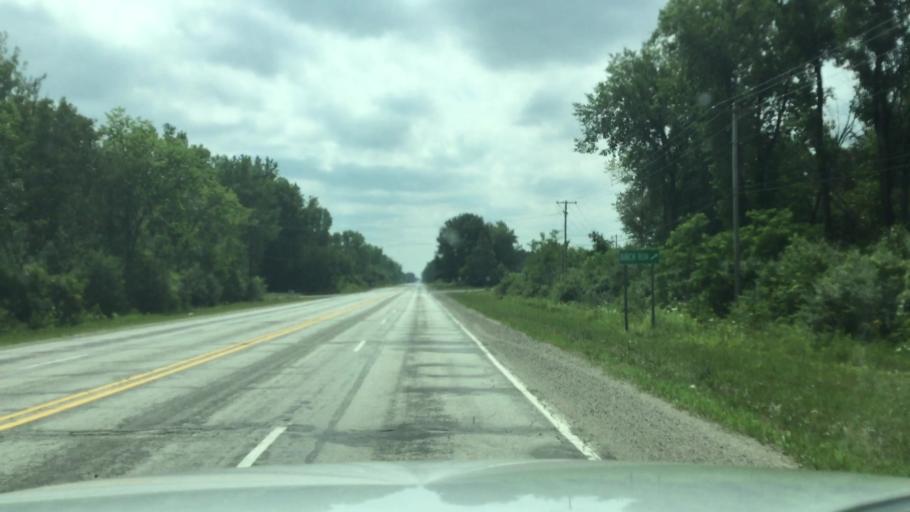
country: US
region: Michigan
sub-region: Saginaw County
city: Birch Run
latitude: 43.2848
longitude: -83.7956
